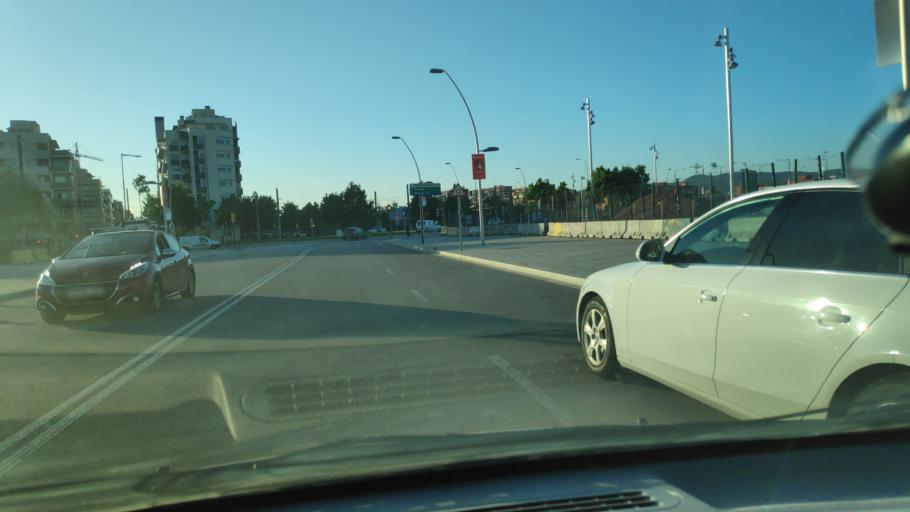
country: ES
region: Catalonia
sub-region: Provincia de Barcelona
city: Sant Adria de Besos
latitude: 41.4222
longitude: 2.2232
